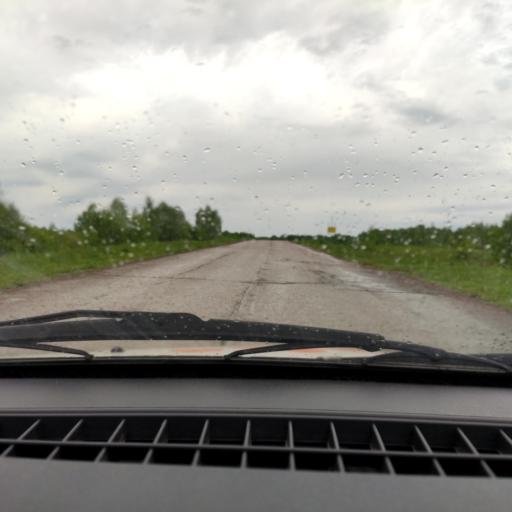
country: RU
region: Bashkortostan
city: Urman
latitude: 54.8548
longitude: 56.8251
